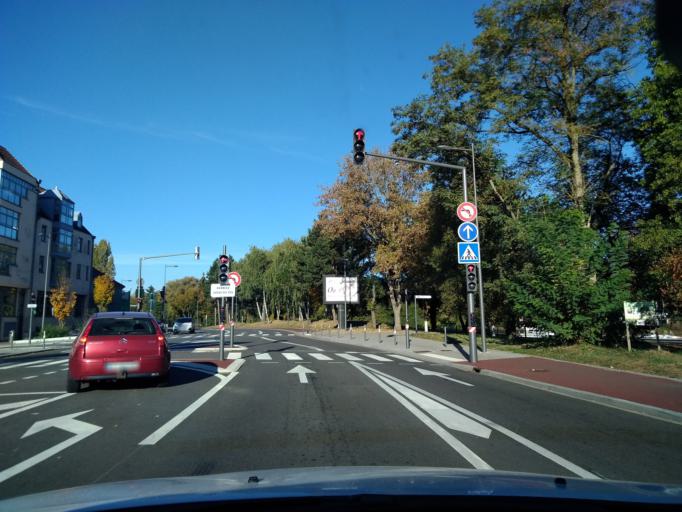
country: FR
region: Lorraine
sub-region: Departement de la Moselle
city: Sarreguemines
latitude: 49.1133
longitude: 7.0669
